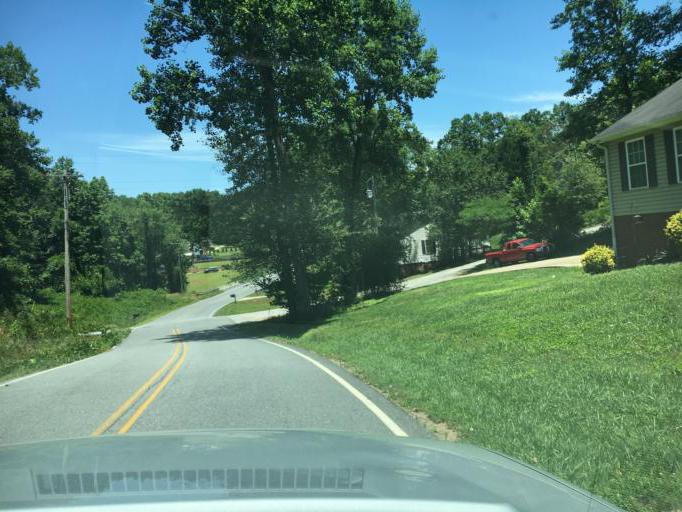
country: US
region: South Carolina
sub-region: Greenville County
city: Greer
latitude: 34.9570
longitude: -82.2235
